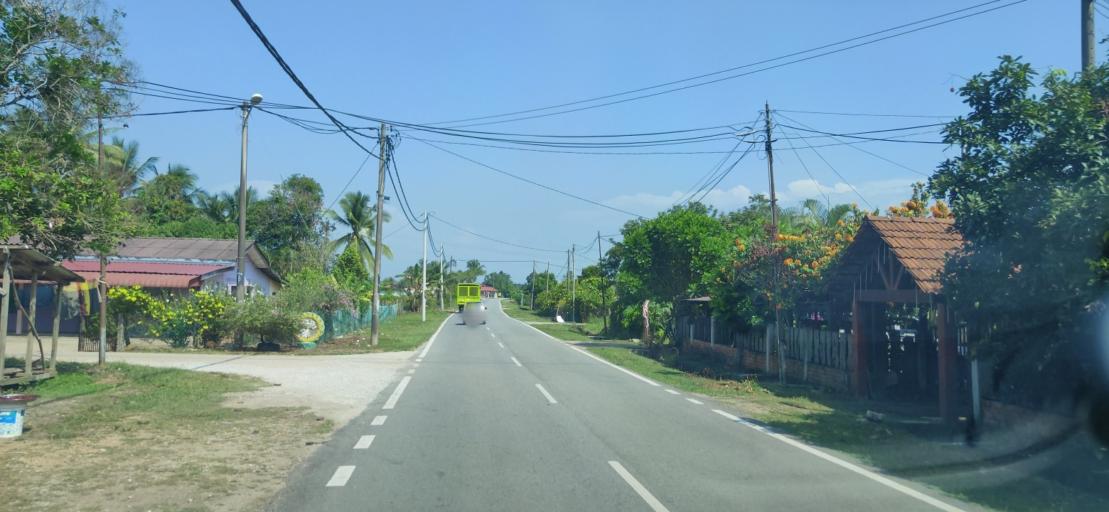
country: MY
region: Kedah
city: Sungai Petani
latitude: 5.6589
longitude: 100.4741
